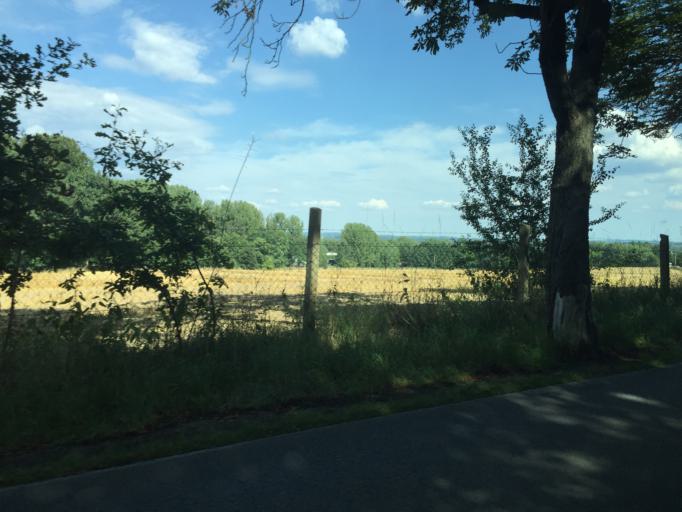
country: DE
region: Saxony
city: Goerlitz
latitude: 51.1276
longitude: 14.9619
